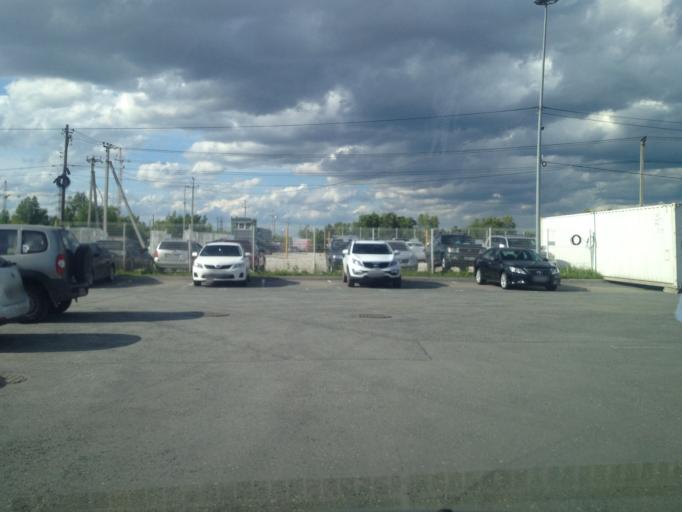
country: RU
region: Sverdlovsk
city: Shirokaya Rechka
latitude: 56.8286
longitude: 60.5274
